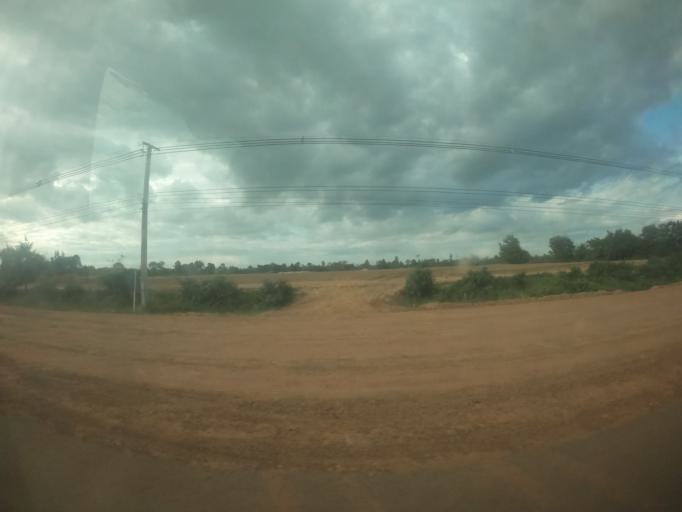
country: TH
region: Surin
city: Kap Choeng
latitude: 14.4598
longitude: 103.6631
